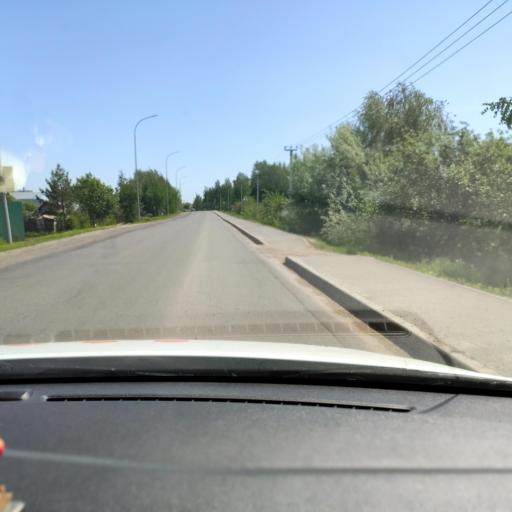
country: RU
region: Tatarstan
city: Stolbishchi
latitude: 55.6954
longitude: 49.1974
